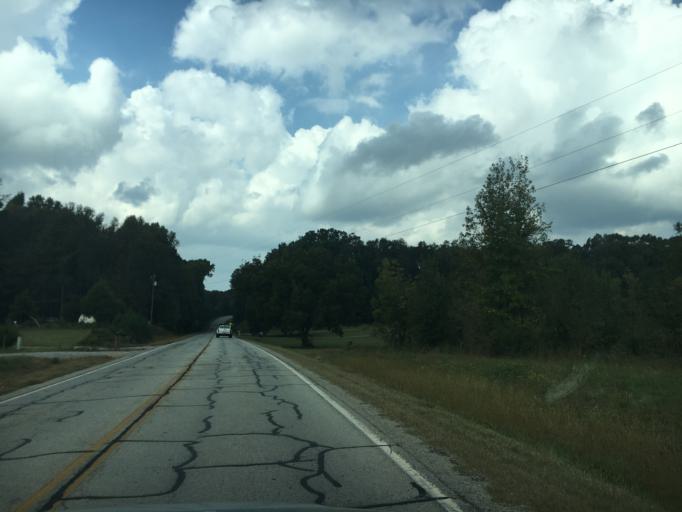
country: US
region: Georgia
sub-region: Hart County
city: Hartwell
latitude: 34.2674
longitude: -82.8957
